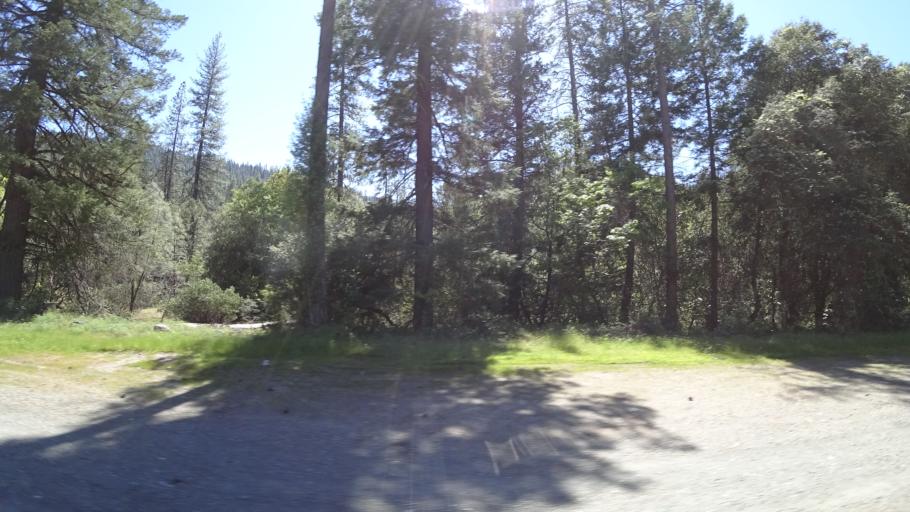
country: US
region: California
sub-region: Trinity County
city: Hayfork
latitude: 40.7403
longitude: -123.2533
